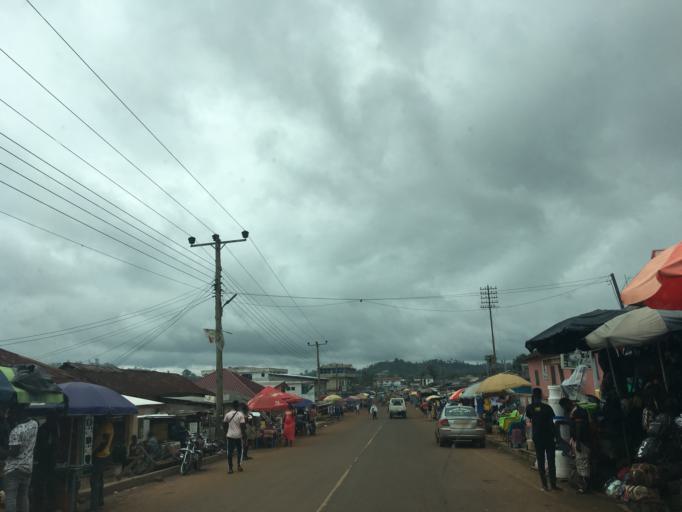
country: GH
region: Western
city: Wassa-Akropong
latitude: 5.8079
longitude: -2.4353
